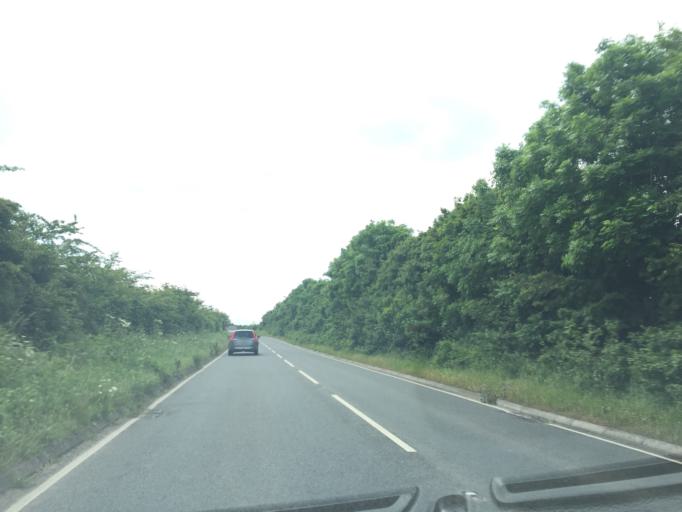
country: GB
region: England
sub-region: Dorset
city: Wool
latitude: 50.6747
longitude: -2.2422
